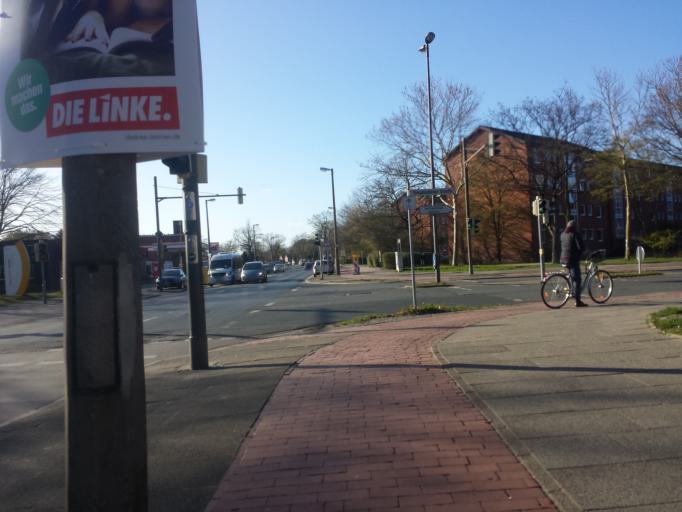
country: DE
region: Lower Saxony
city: Lilienthal
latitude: 53.0663
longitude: 8.9439
